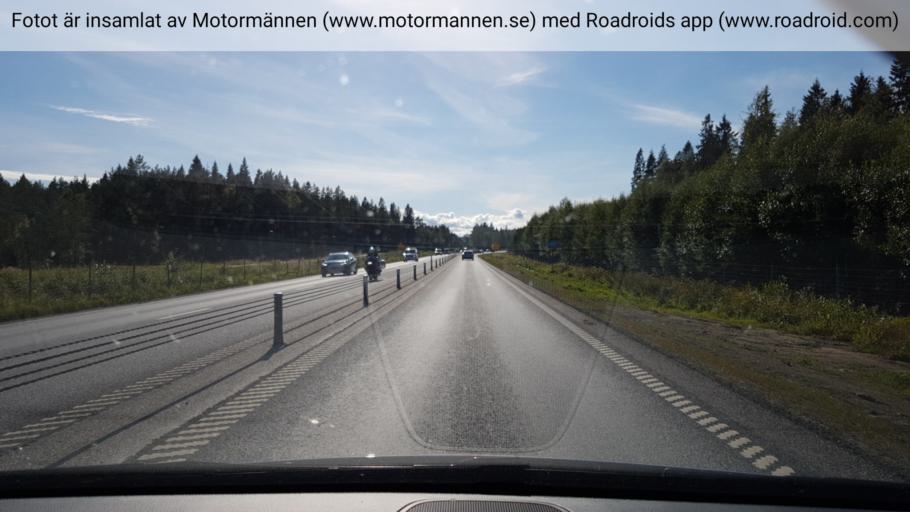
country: SE
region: Vaesterbotten
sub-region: Umea Kommun
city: Ersmark
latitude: 63.8495
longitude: 20.3563
